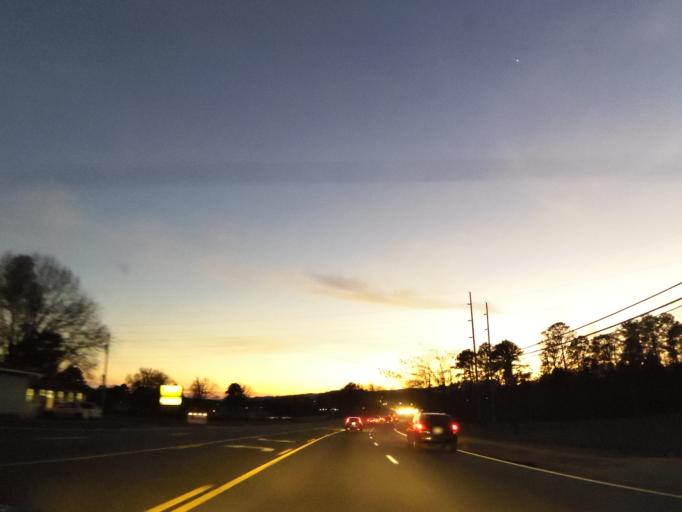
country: US
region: Georgia
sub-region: Whitfield County
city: Dalton
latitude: 34.8110
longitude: -84.9490
